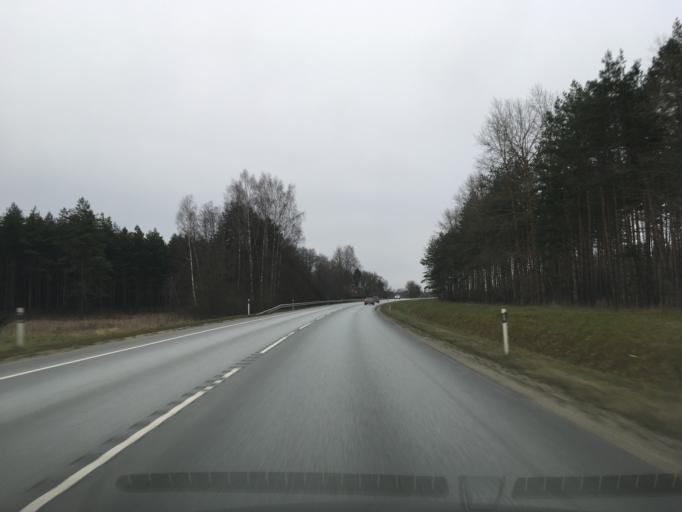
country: EE
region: Laeaene-Virumaa
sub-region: Viru-Nigula vald
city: Kunda
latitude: 59.4069
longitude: 26.6377
